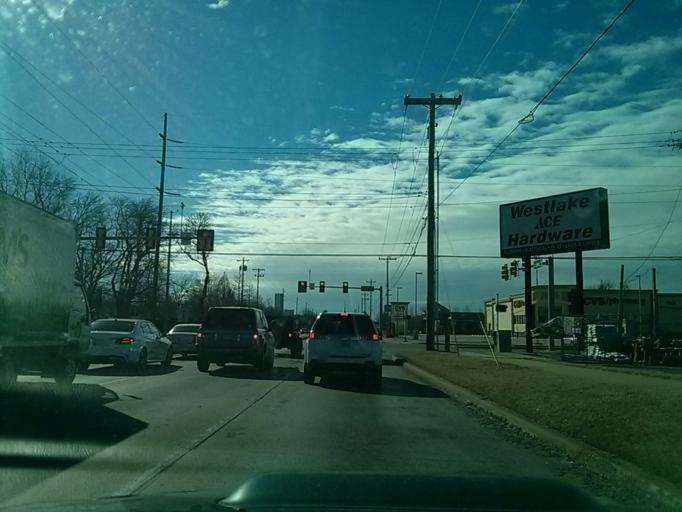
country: US
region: Oklahoma
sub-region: Tulsa County
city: Jenks
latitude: 36.0758
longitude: -95.9579
